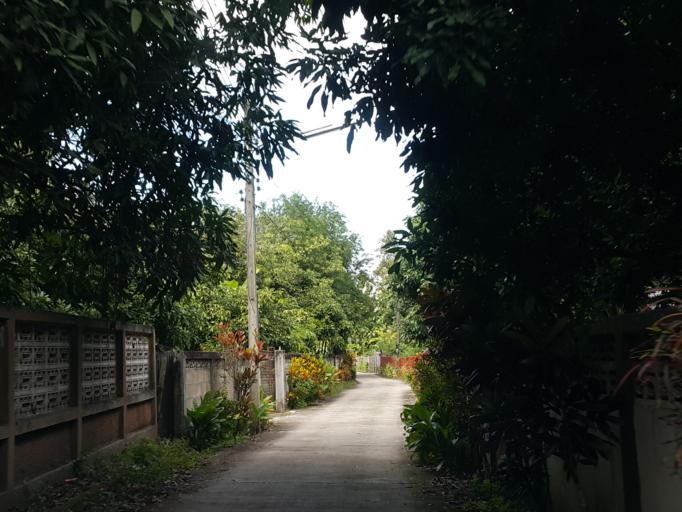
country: TH
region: Lampang
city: Chae Hom
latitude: 18.6435
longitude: 99.5407
